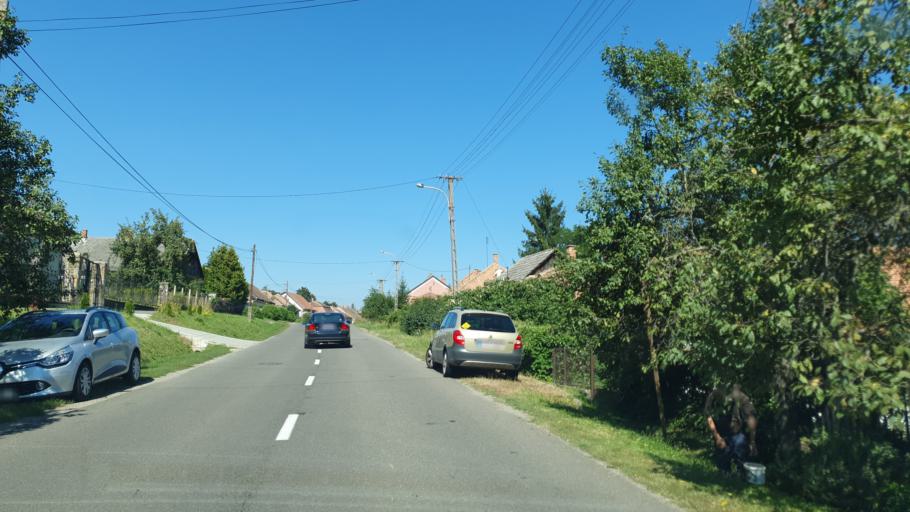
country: HU
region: Nograd
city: Rimoc
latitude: 48.0294
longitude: 19.5800
